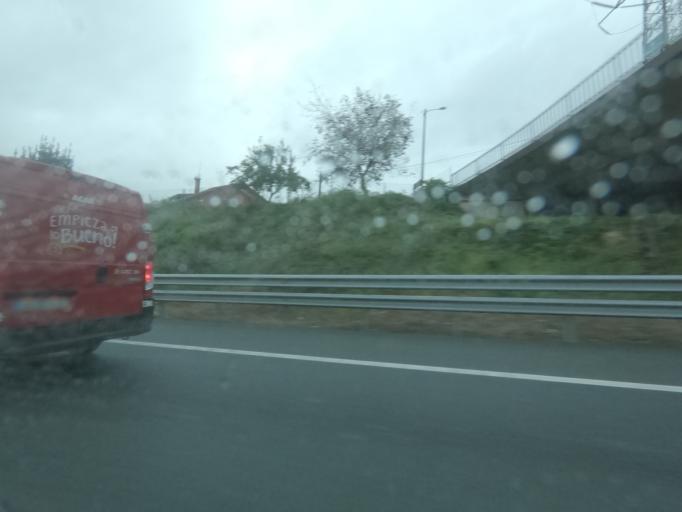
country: ES
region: Galicia
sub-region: Provincia de Pontevedra
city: Poio
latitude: 42.4042
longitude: -8.6504
